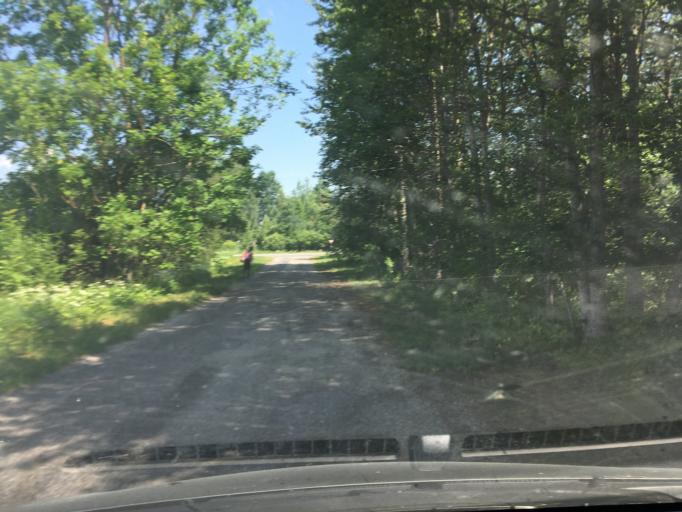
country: EE
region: Laeaene
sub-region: Lihula vald
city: Lihula
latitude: 58.6679
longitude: 23.7653
